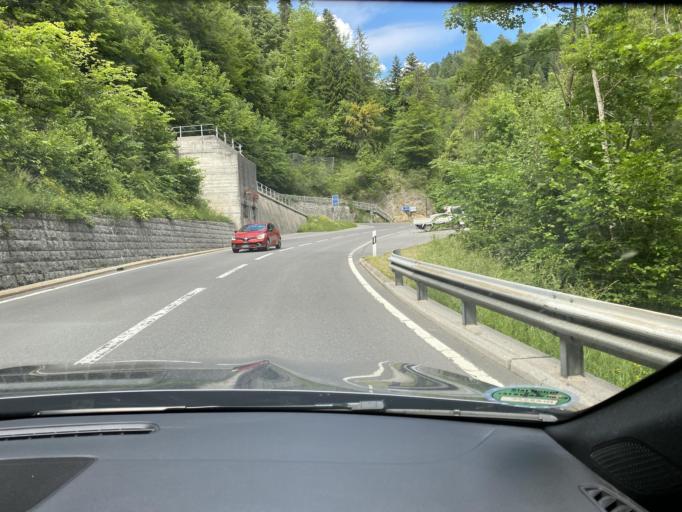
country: CH
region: Vaud
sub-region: Aigle District
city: Leysin
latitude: 46.3619
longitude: 7.0500
